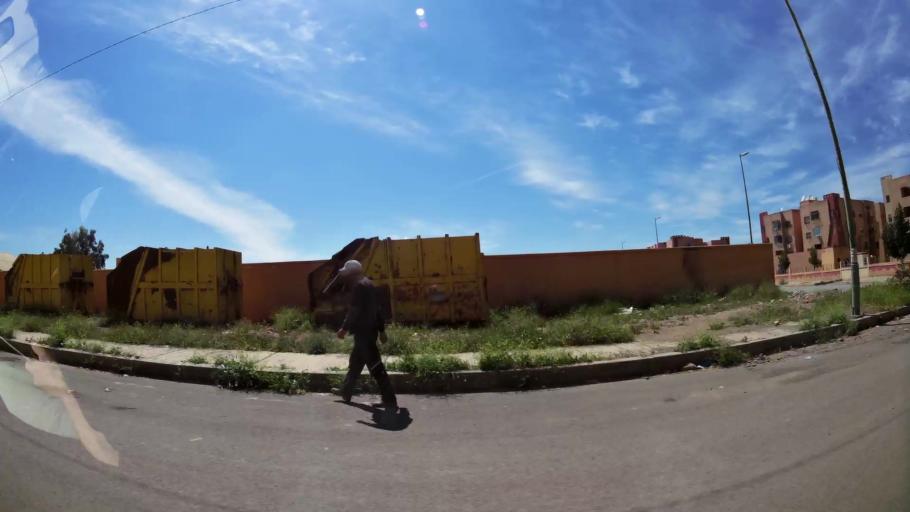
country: MA
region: Marrakech-Tensift-Al Haouz
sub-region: Marrakech
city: Marrakesh
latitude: 31.6336
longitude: -8.0760
